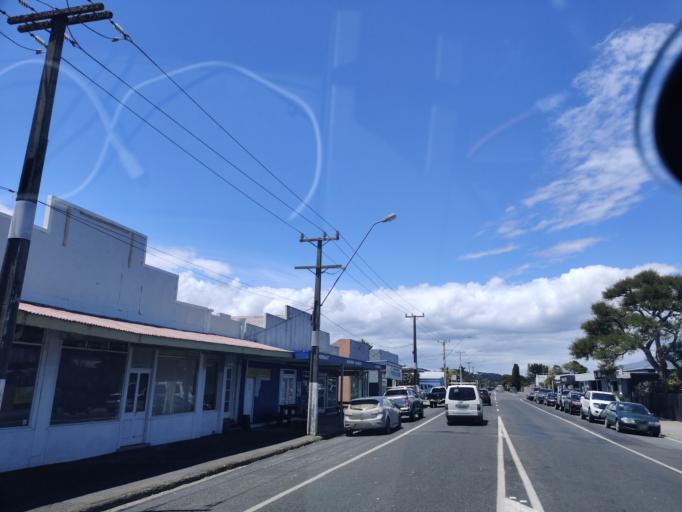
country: NZ
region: Northland
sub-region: Far North District
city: Kaitaia
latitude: -35.0478
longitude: 173.2563
